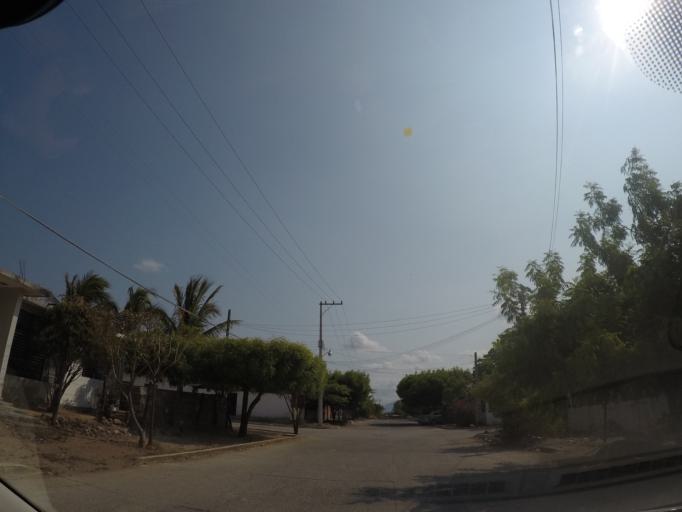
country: MX
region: Oaxaca
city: San Jeronimo Ixtepec
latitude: 16.5469
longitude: -95.0896
